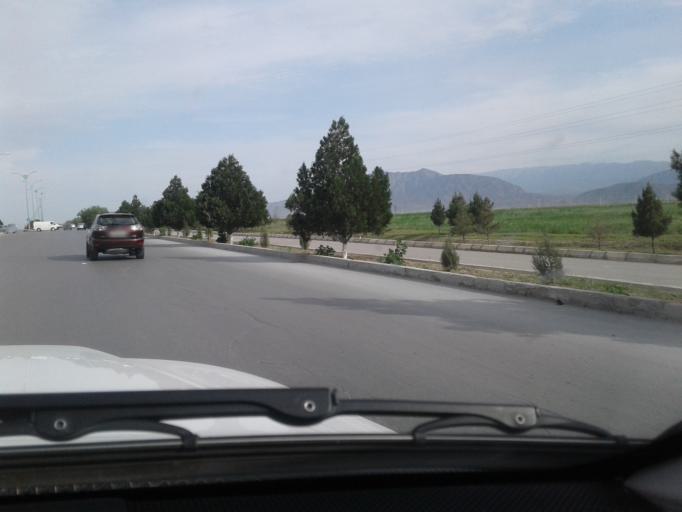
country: TM
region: Ahal
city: Abadan
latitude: 38.1510
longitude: 57.9817
